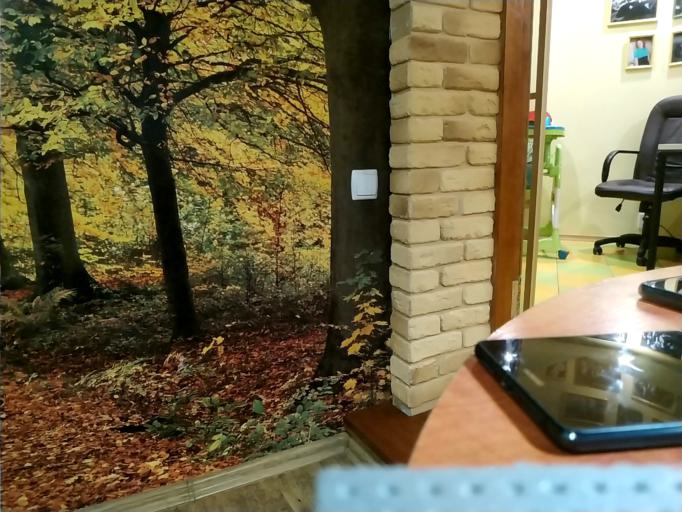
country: RU
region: Tverskaya
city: Zubtsov
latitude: 56.2265
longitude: 34.7087
